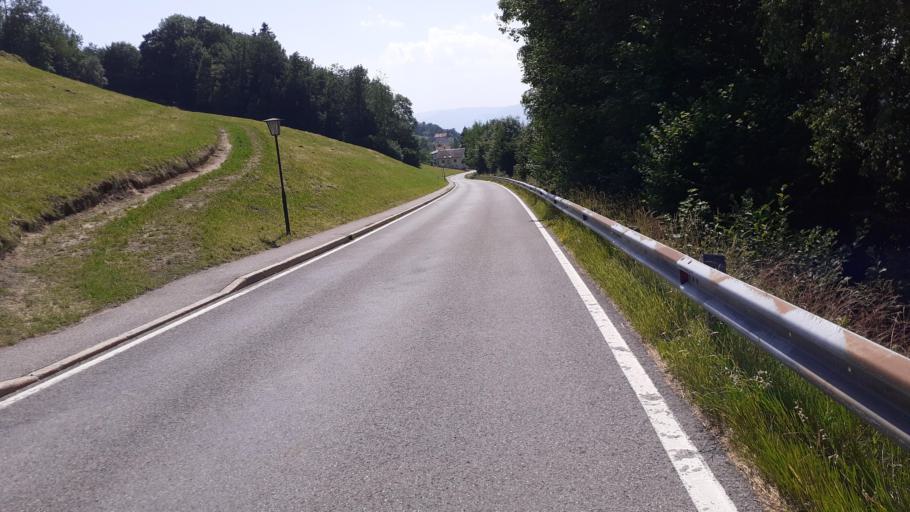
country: AT
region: Vorarlberg
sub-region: Politischer Bezirk Bregenz
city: Kennelbach
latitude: 47.4859
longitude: 9.8189
